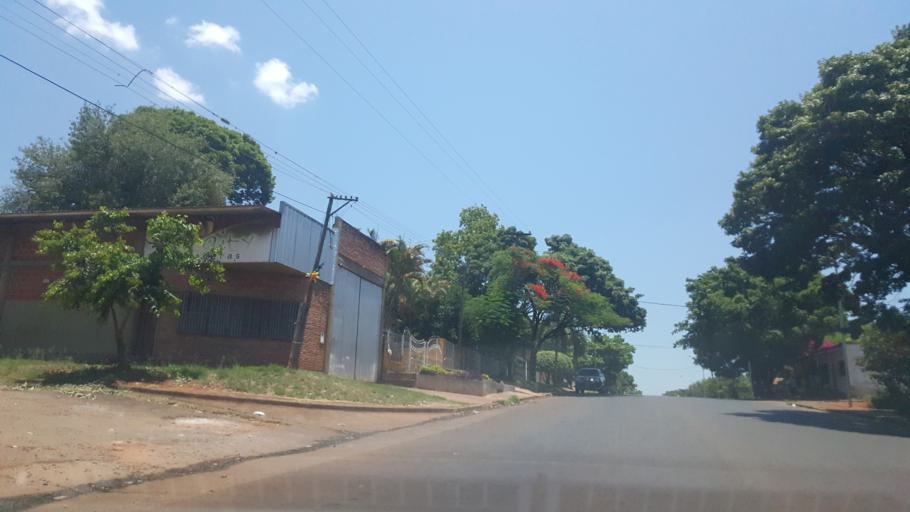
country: AR
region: Misiones
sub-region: Departamento de Capital
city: Posadas
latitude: -27.4052
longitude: -55.8963
